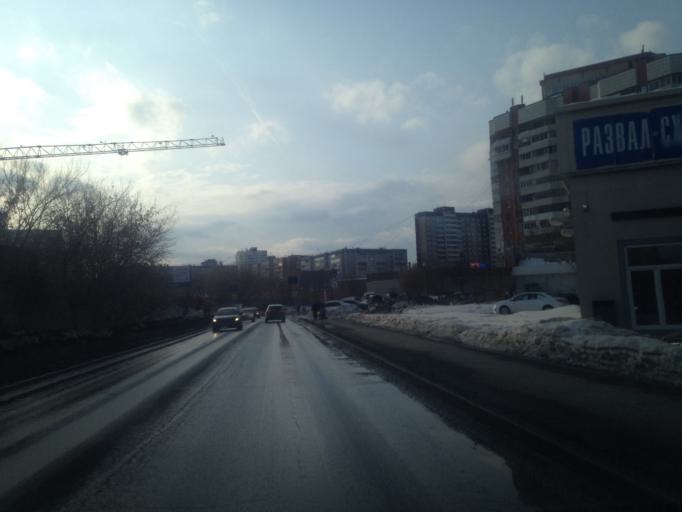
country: RU
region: Sverdlovsk
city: Yekaterinburg
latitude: 56.8529
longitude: 60.5766
